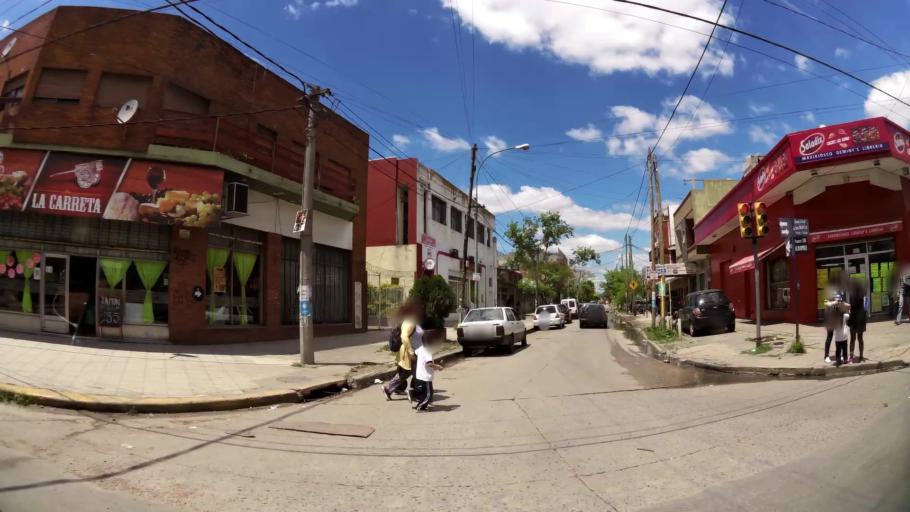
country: AR
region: Buenos Aires
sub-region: Partido de Lanus
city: Lanus
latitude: -34.7077
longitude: -58.4185
